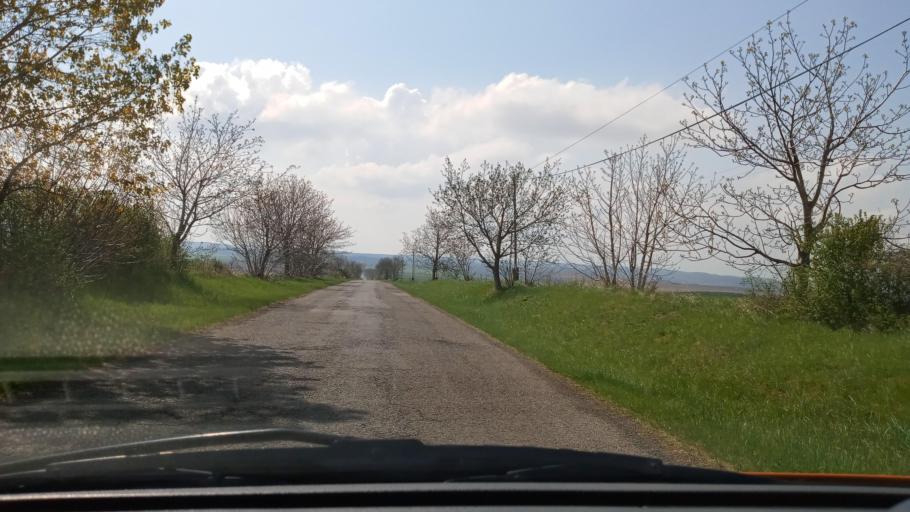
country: HU
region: Baranya
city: Pecsvarad
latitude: 46.1028
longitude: 18.4964
